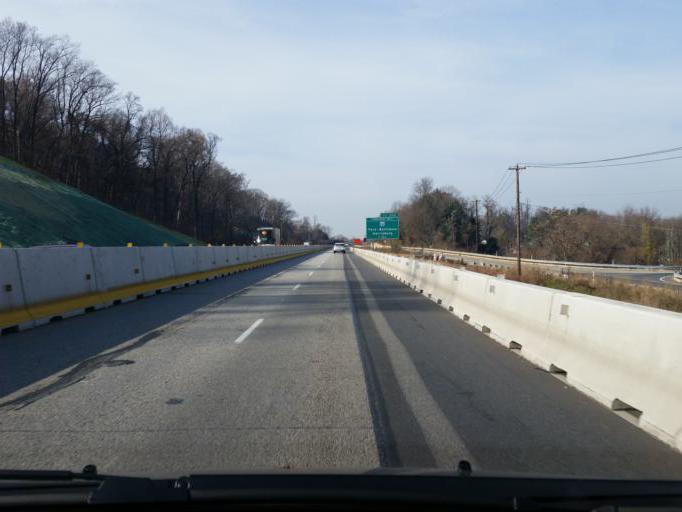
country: US
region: Pennsylvania
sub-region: Dauphin County
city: Steelton
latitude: 40.2060
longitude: -76.8554
